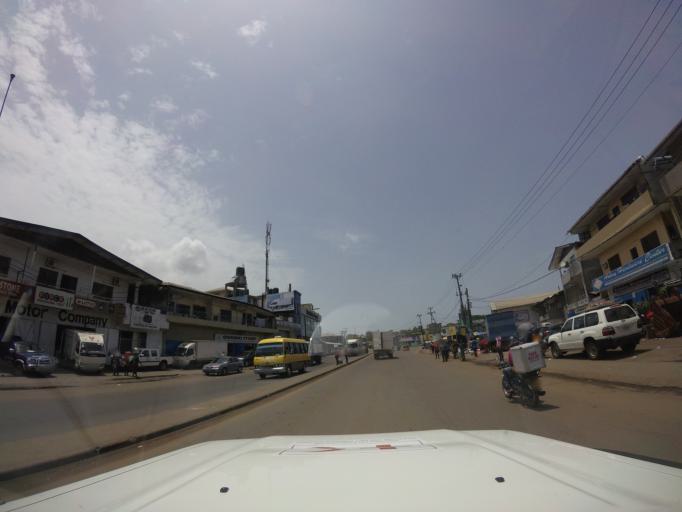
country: LR
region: Montserrado
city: Monrovia
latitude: 6.3240
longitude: -10.8019
